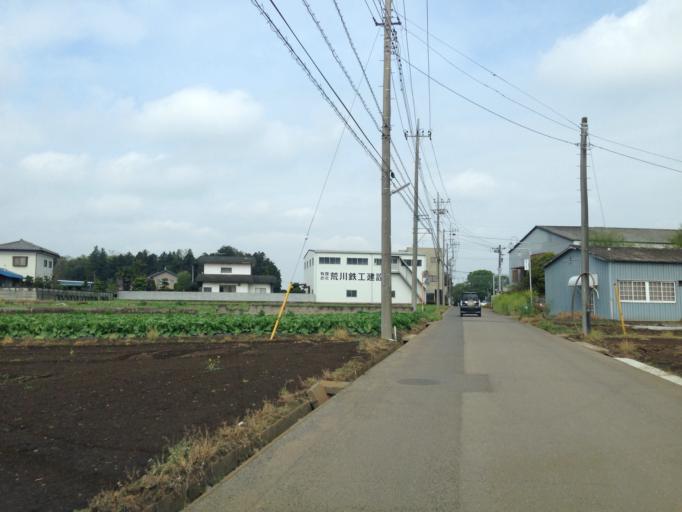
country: JP
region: Ibaraki
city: Sakai
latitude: 36.1617
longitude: 139.8340
